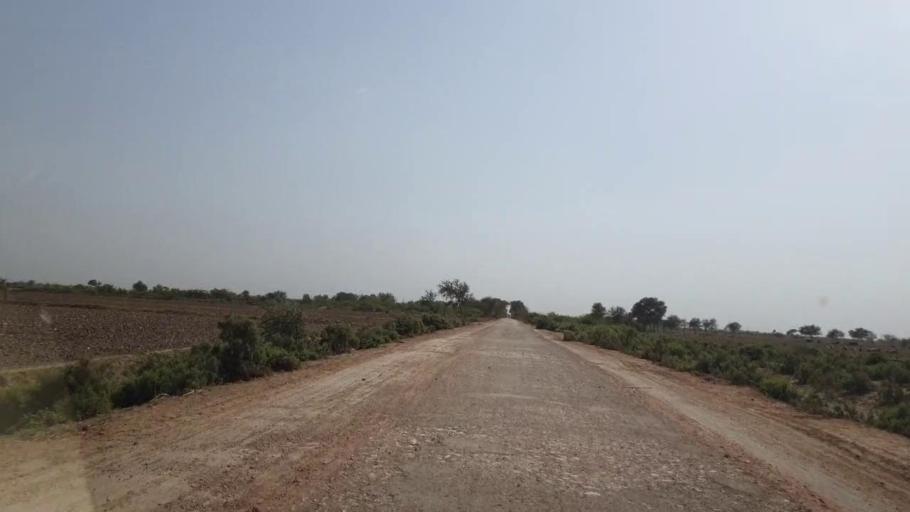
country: PK
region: Sindh
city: Rajo Khanani
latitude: 25.0348
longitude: 68.8730
